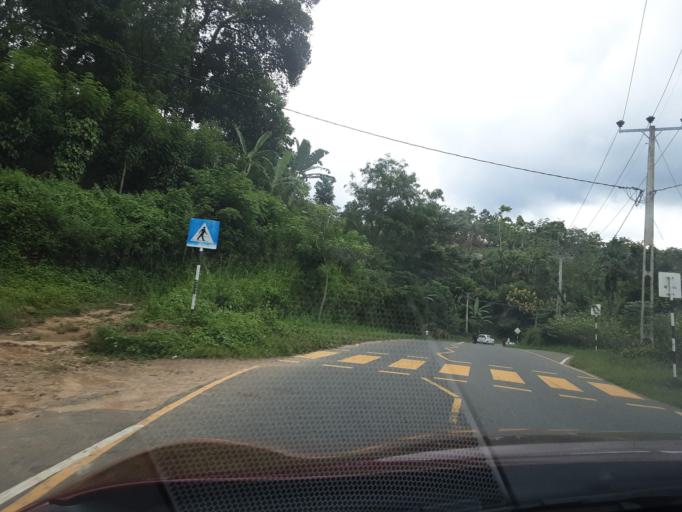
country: LK
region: Uva
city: Monaragala
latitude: 6.9066
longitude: 81.2100
